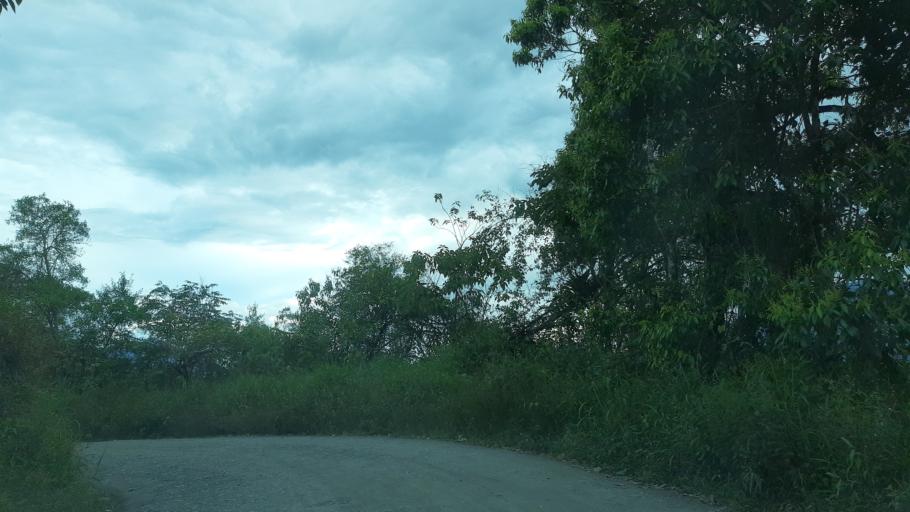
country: CO
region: Boyaca
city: Garagoa
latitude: 4.9835
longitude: -73.3229
